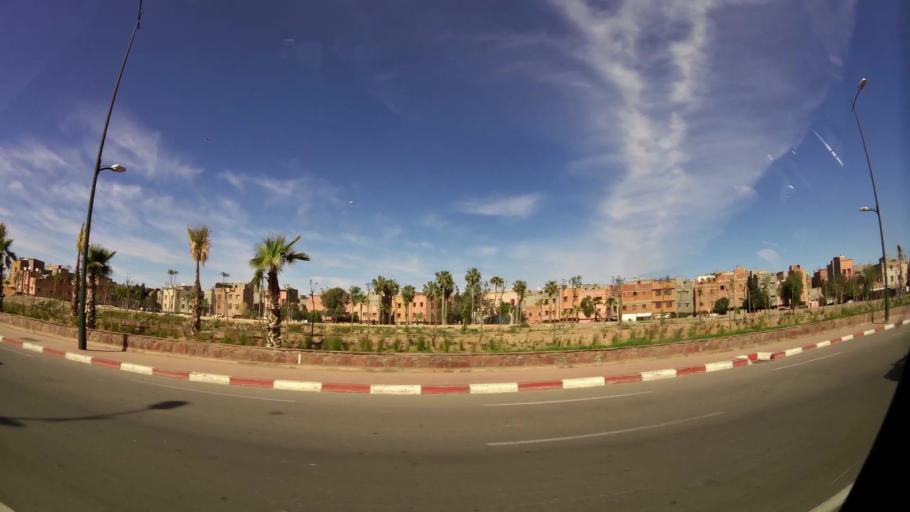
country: MA
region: Marrakech-Tensift-Al Haouz
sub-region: Marrakech
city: Marrakesh
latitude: 31.6361
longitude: -7.9790
